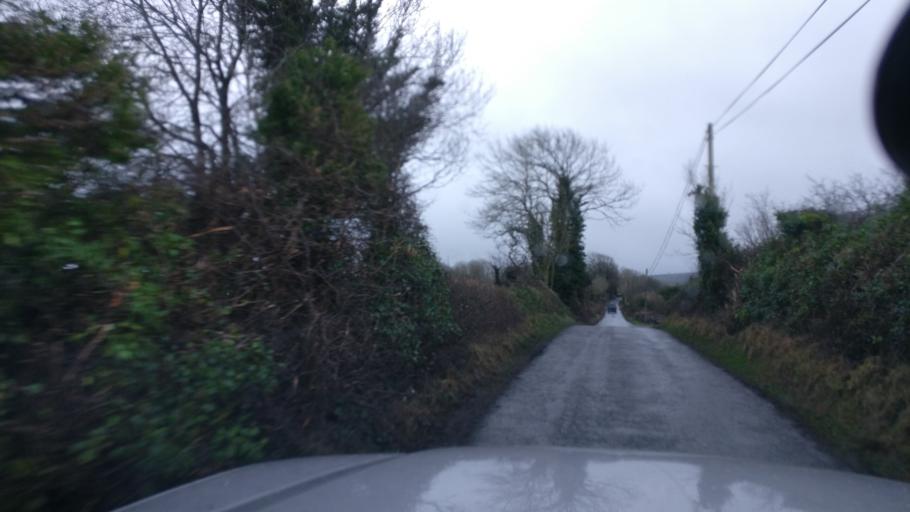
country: IE
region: Connaught
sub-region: County Galway
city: Loughrea
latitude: 53.1927
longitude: -8.6624
